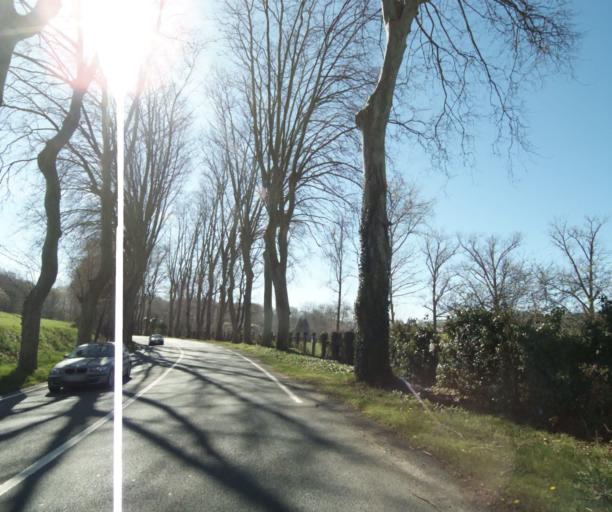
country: FR
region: Aquitaine
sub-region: Departement des Pyrenees-Atlantiques
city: Urrugne
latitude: 43.3683
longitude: -1.6859
